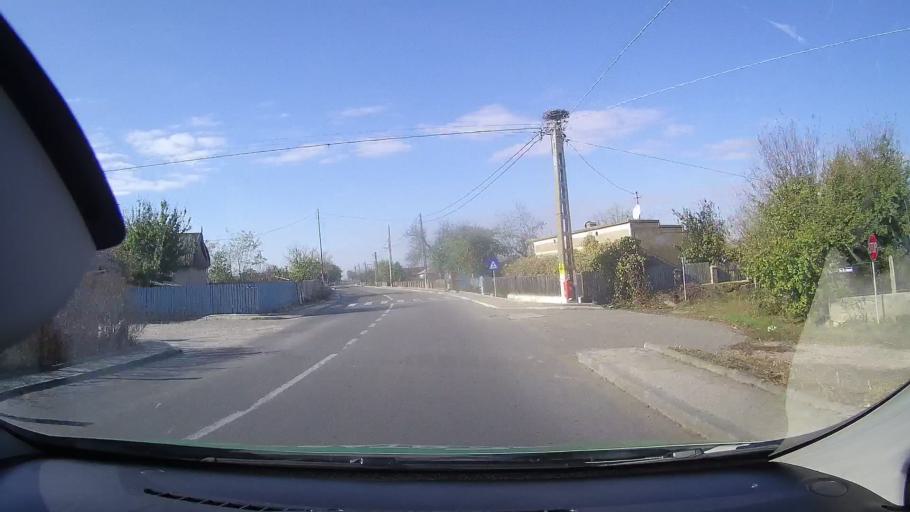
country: RO
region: Tulcea
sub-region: Comuna Murighiol
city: Murighiol
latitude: 45.0199
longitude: 29.1167
